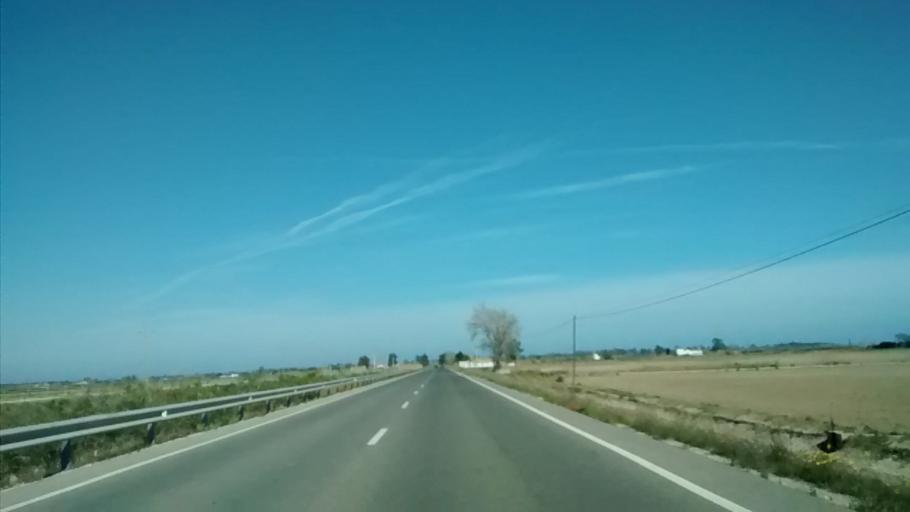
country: ES
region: Catalonia
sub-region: Provincia de Tarragona
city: Deltebre
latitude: 40.7050
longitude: 0.7970
